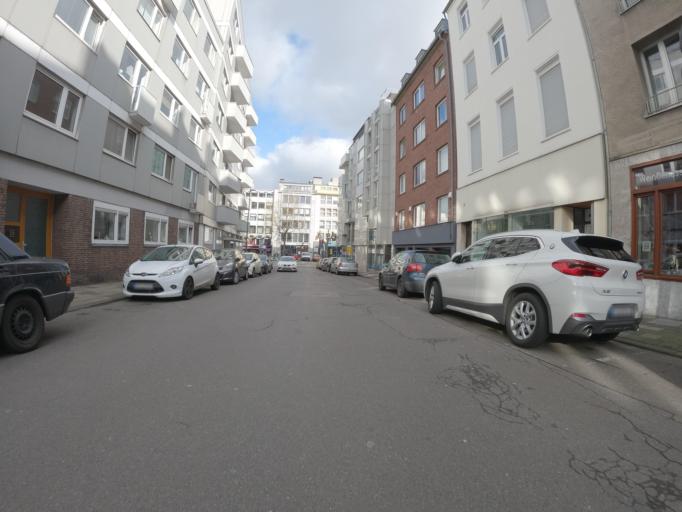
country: DE
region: North Rhine-Westphalia
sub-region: Regierungsbezirk Koln
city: Aachen
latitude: 50.7707
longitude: 6.0903
